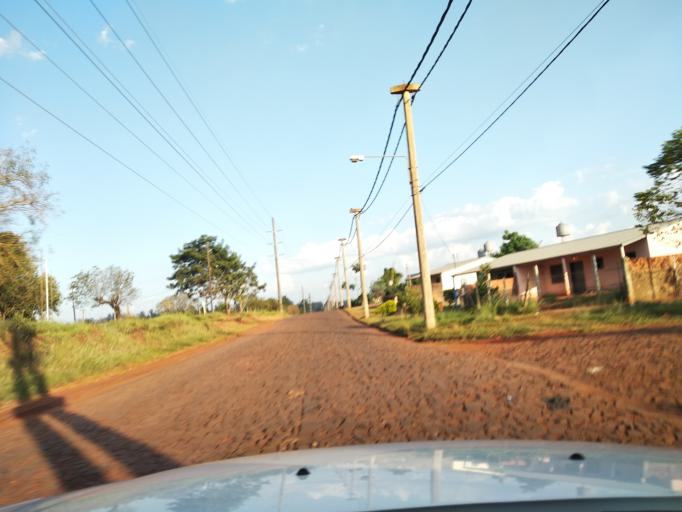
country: AR
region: Misiones
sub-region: Departamento de Capital
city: Posadas
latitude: -27.4421
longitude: -55.9431
